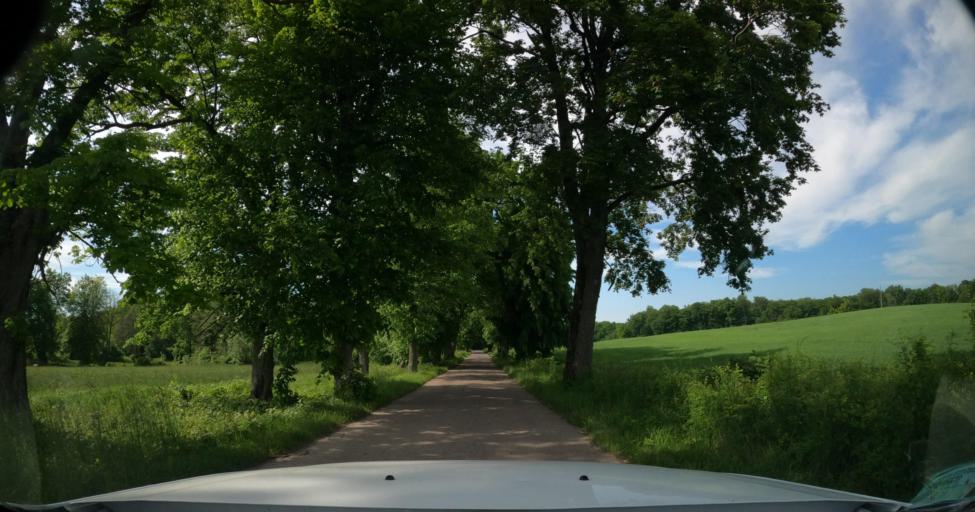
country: PL
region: Warmian-Masurian Voivodeship
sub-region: Powiat ostrodzki
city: Morag
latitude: 54.0228
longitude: 19.9131
